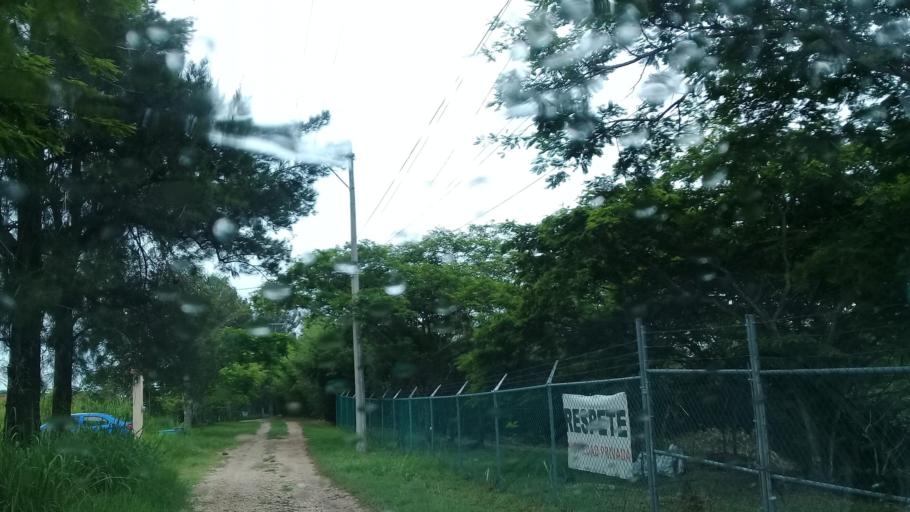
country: MX
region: Veracruz
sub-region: Emiliano Zapata
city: Jacarandas
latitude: 19.5095
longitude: -96.8390
